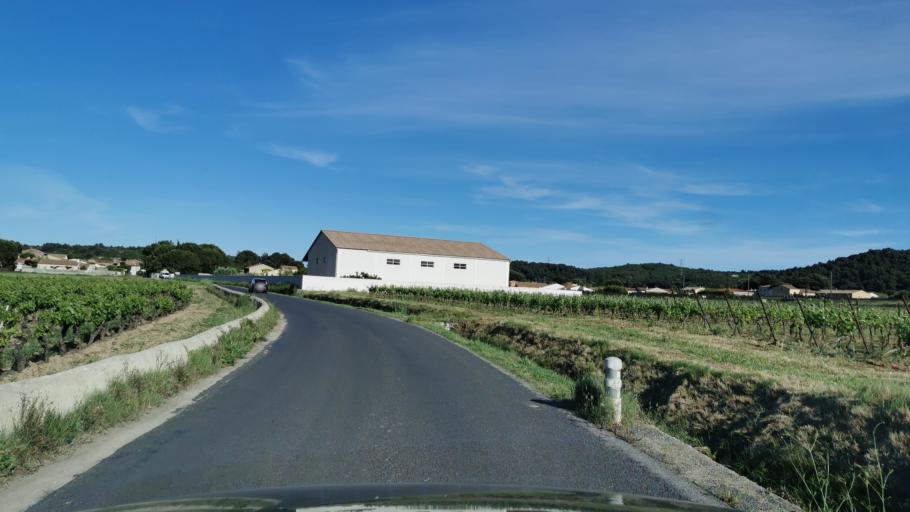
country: FR
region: Languedoc-Roussillon
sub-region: Departement de l'Aude
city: Nevian
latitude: 43.2127
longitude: 2.8950
